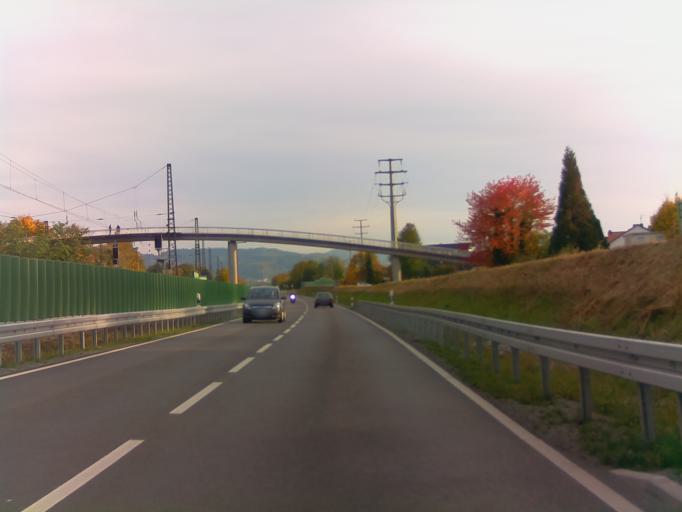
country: DE
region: Baden-Wuerttemberg
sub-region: Karlsruhe Region
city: Hemsbach
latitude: 49.5877
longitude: 8.6494
